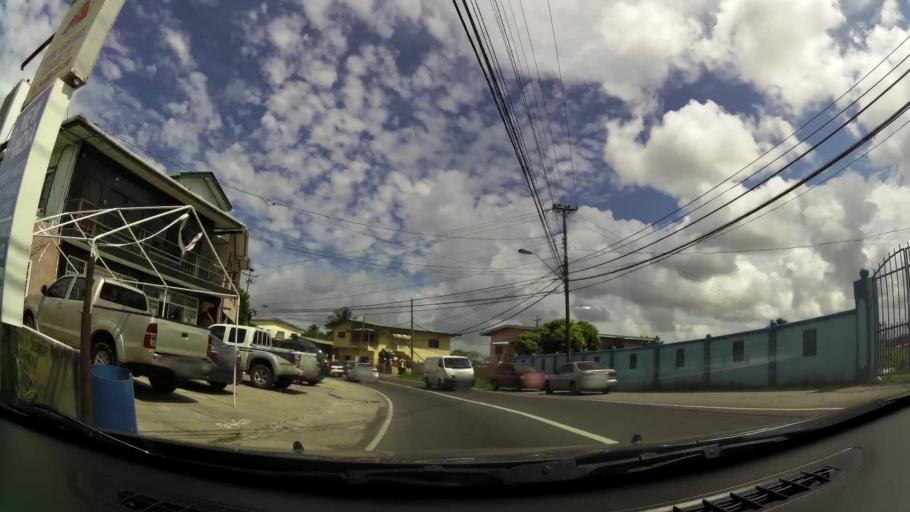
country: TT
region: City of San Fernando
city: Marabella
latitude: 10.2977
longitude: -61.4521
